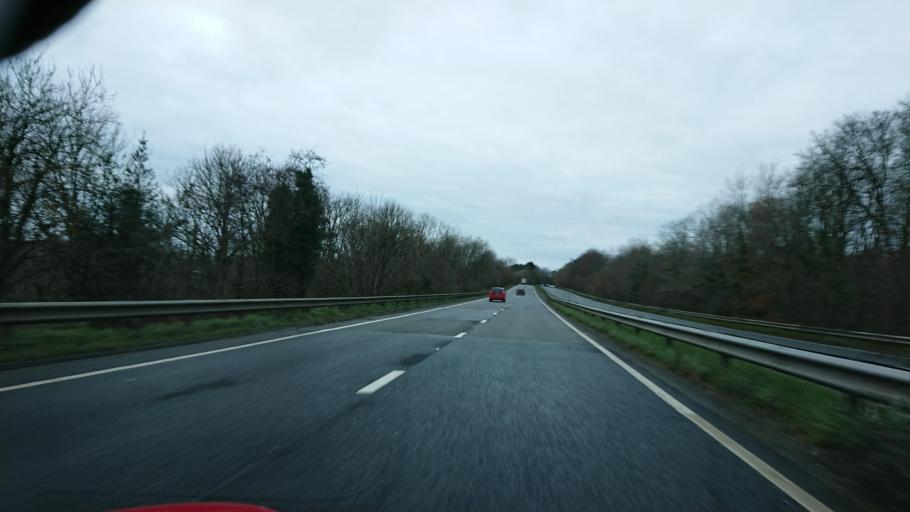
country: GB
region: England
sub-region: Cornwall
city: Liskeard
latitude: 50.4502
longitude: -4.4590
